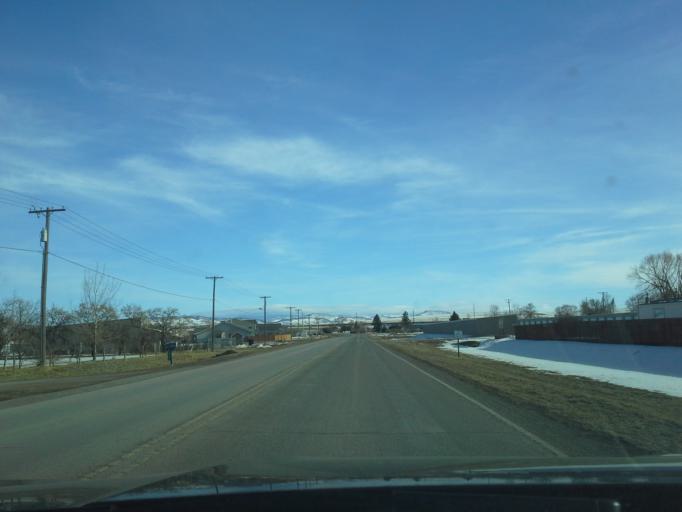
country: US
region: Montana
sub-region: Lewis and Clark County
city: East Helena
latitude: 46.5886
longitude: -111.9015
